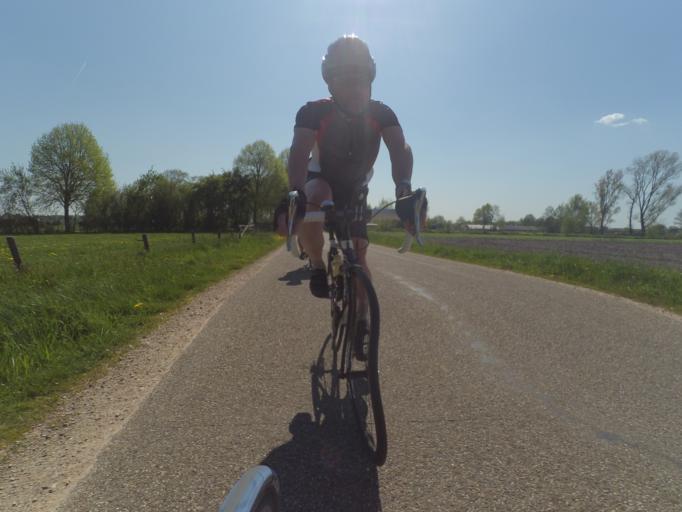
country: NL
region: Gelderland
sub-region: Gemeente Apeldoorn
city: Uddel
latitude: 52.2656
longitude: 5.7674
